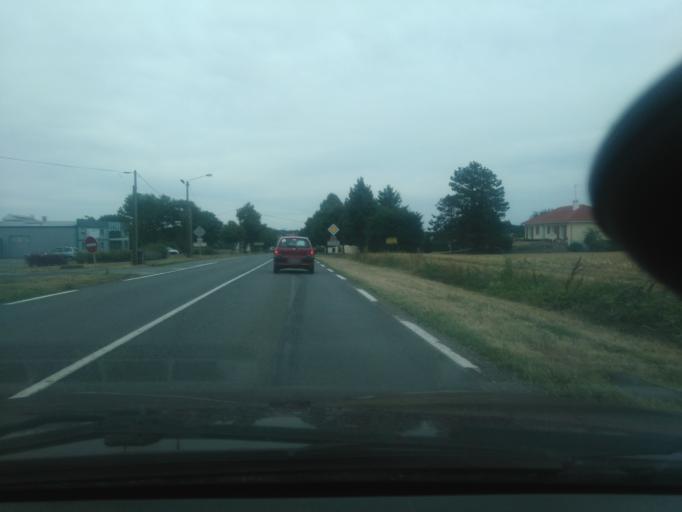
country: FR
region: Poitou-Charentes
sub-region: Departement de la Vienne
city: Ayron
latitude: 46.6596
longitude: 0.0609
